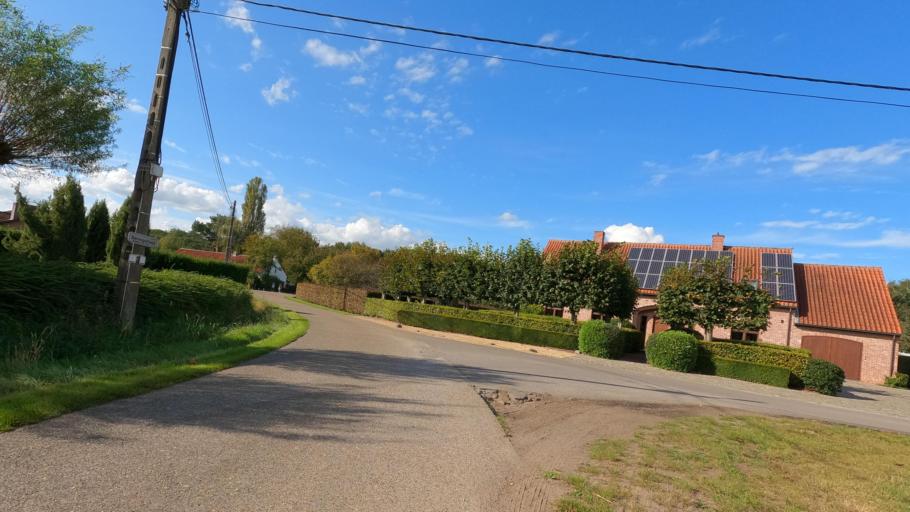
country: BE
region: Flanders
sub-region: Provincie Antwerpen
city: Herselt
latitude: 51.0434
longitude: 4.8809
